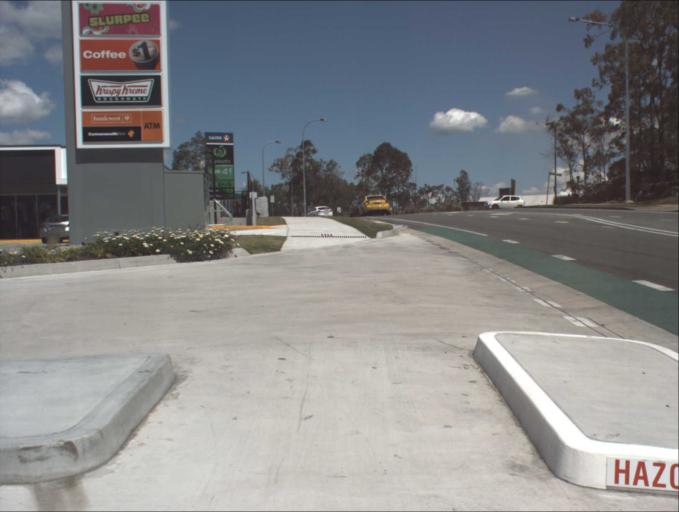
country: AU
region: Queensland
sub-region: Logan
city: Waterford West
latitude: -27.7096
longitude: 153.1605
